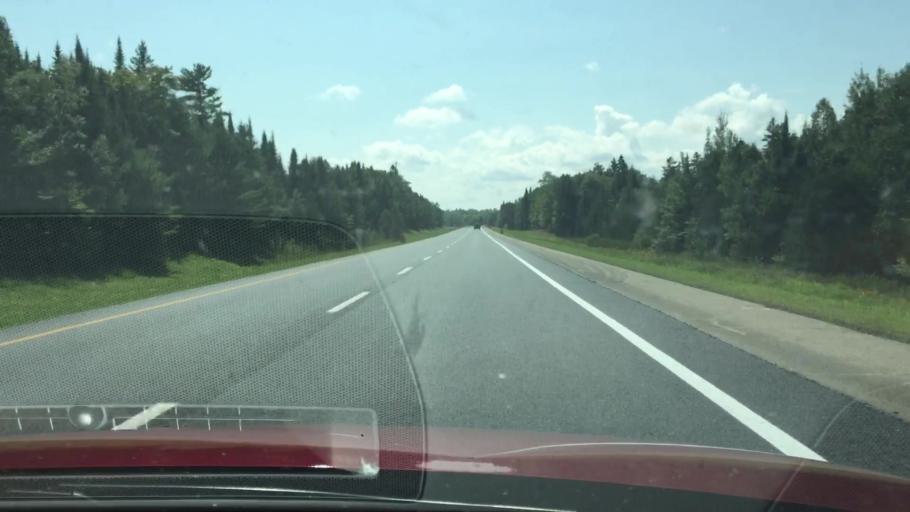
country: US
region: Maine
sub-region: Penobscot County
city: Patten
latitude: 45.8494
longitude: -68.4288
